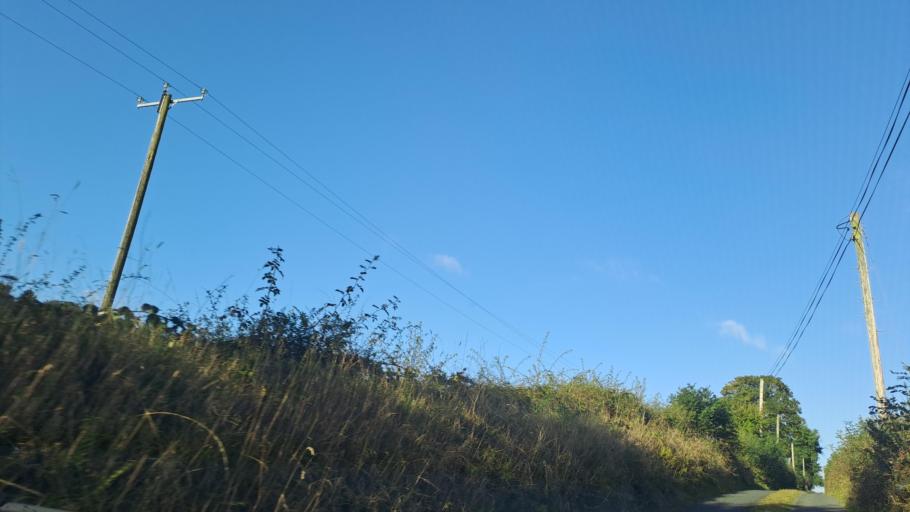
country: IE
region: Ulster
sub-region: An Cabhan
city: Kingscourt
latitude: 53.9889
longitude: -6.8664
